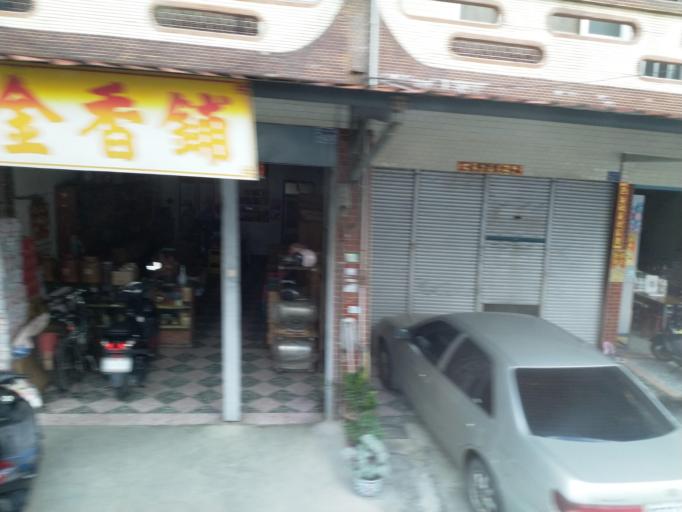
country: TW
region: Taiwan
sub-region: Pingtung
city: Pingtung
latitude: 22.8723
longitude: 120.5366
